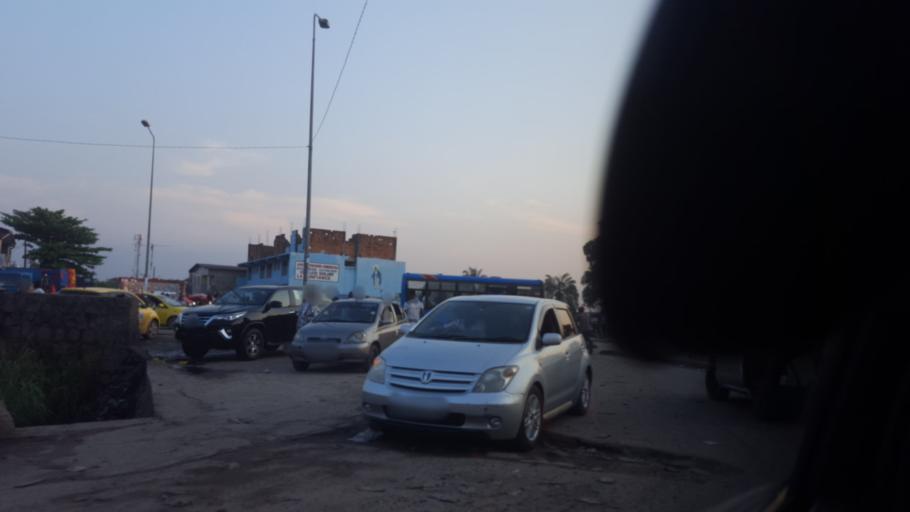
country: CD
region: Kinshasa
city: Kinshasa
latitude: -4.3424
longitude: 15.3197
